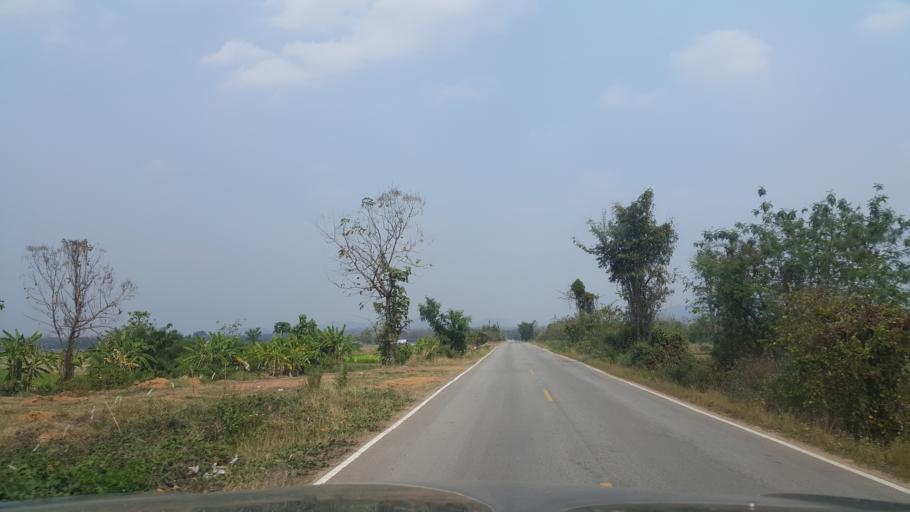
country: TH
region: Lampang
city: Soem Ngam
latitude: 18.0098
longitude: 99.2071
